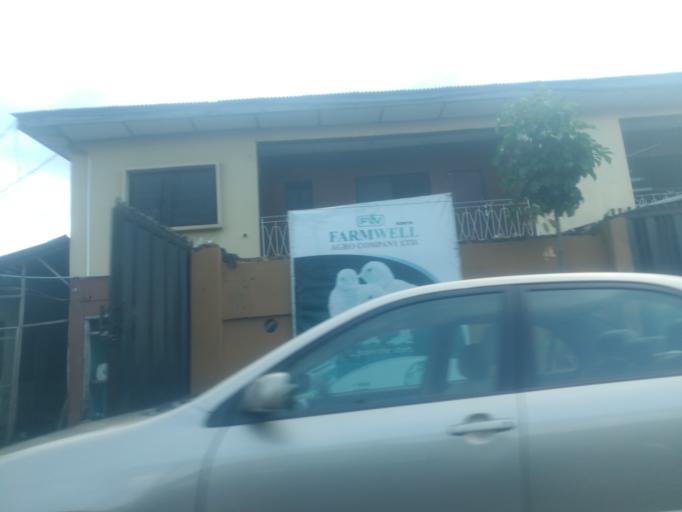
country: NG
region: Oyo
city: Ibadan
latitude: 7.3659
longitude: 3.8532
